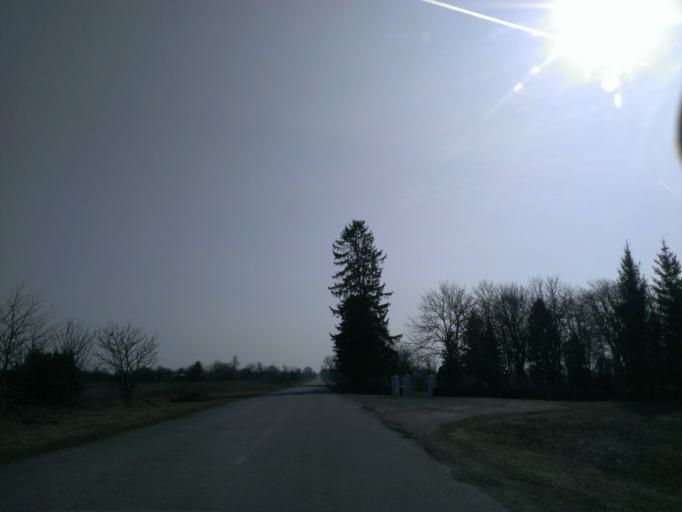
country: EE
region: Saare
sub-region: Orissaare vald
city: Orissaare
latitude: 58.5011
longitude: 23.1143
